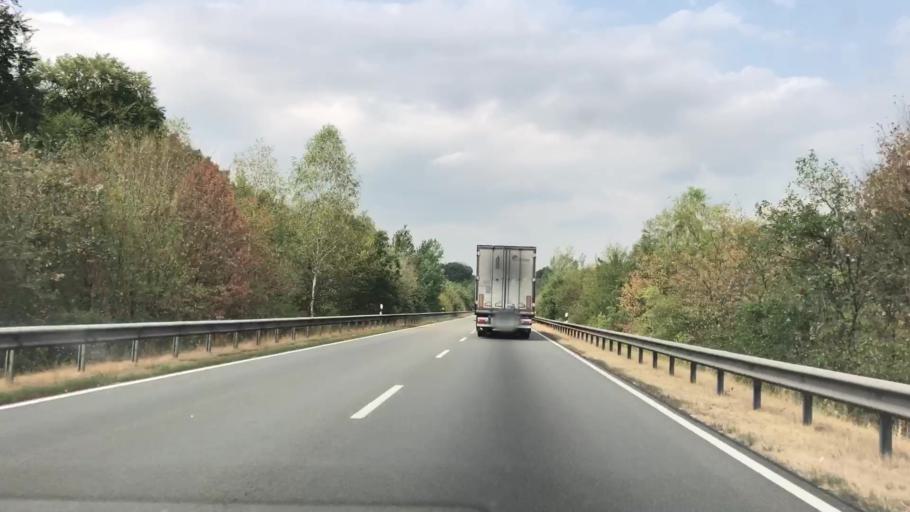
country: DE
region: Lower Saxony
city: Meppen
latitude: 52.7156
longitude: 7.2897
